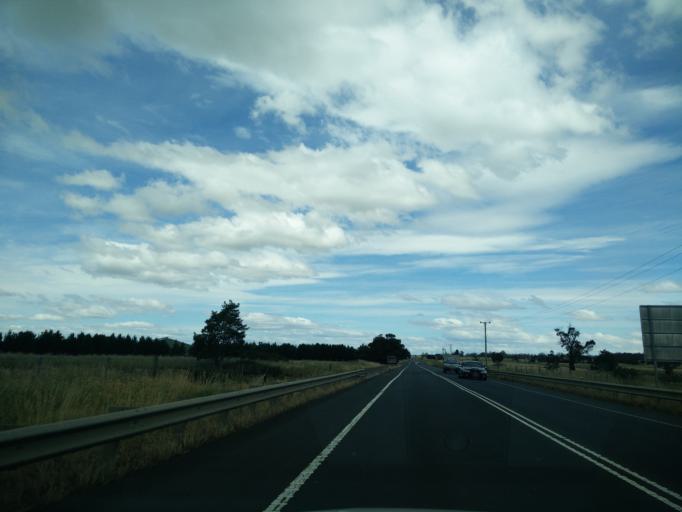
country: AU
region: Tasmania
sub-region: Northern Midlands
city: Evandale
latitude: -41.6818
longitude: 147.2732
